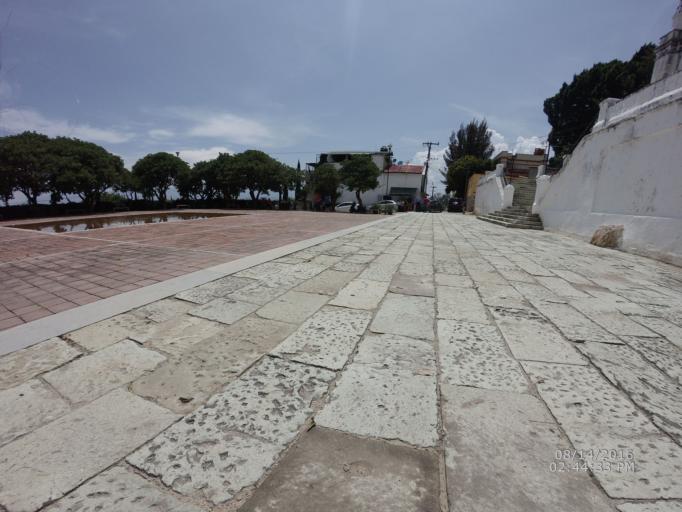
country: MX
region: Oaxaca
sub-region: San Juan Bautista Guelache
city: Fraccionamiento San Miguel
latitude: 17.1969
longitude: -96.7612
